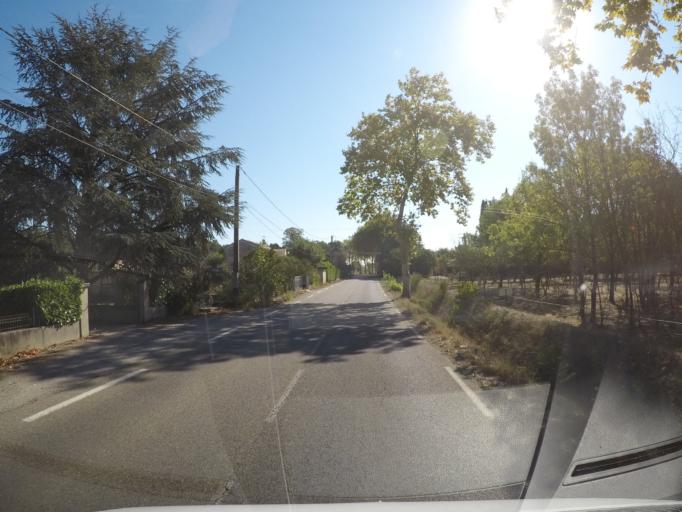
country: FR
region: Languedoc-Roussillon
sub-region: Departement du Gard
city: Ribaute-les-Tavernes
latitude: 44.0244
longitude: 4.0742
